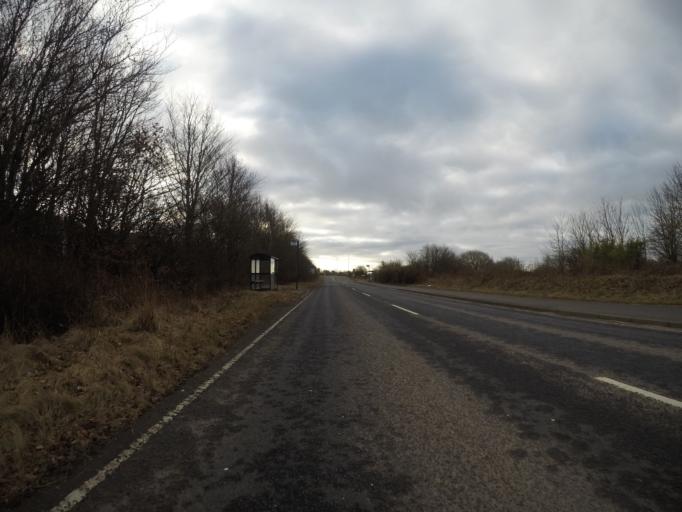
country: GB
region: Scotland
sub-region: North Ayrshire
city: Dreghorn
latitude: 55.5778
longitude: -4.6427
